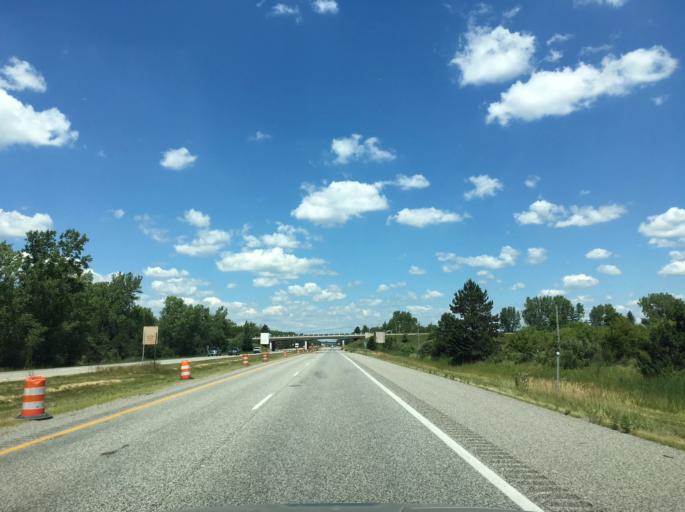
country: US
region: Michigan
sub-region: Midland County
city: Midland
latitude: 43.6243
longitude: -84.1752
